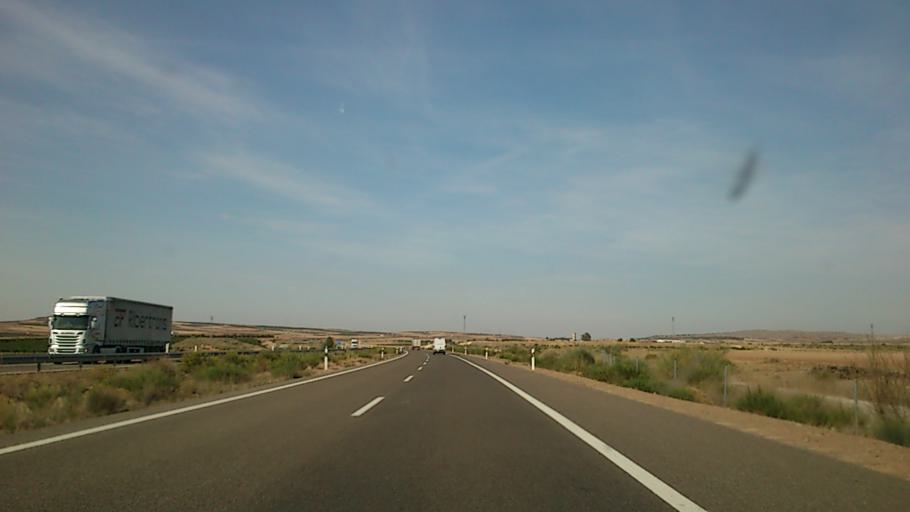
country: ES
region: Aragon
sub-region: Provincia de Zaragoza
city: Longares
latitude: 41.3871
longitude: -1.1852
